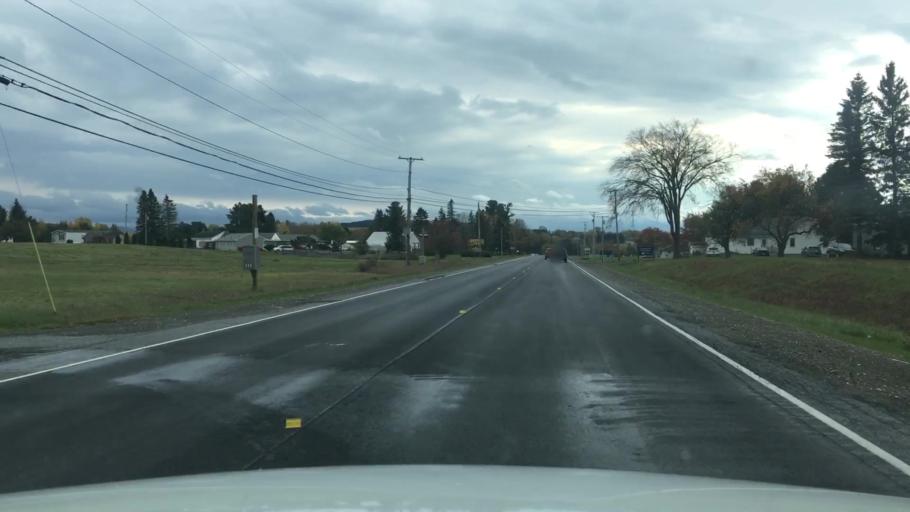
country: US
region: Maine
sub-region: Aroostook County
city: Presque Isle
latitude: 46.6564
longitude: -68.0061
